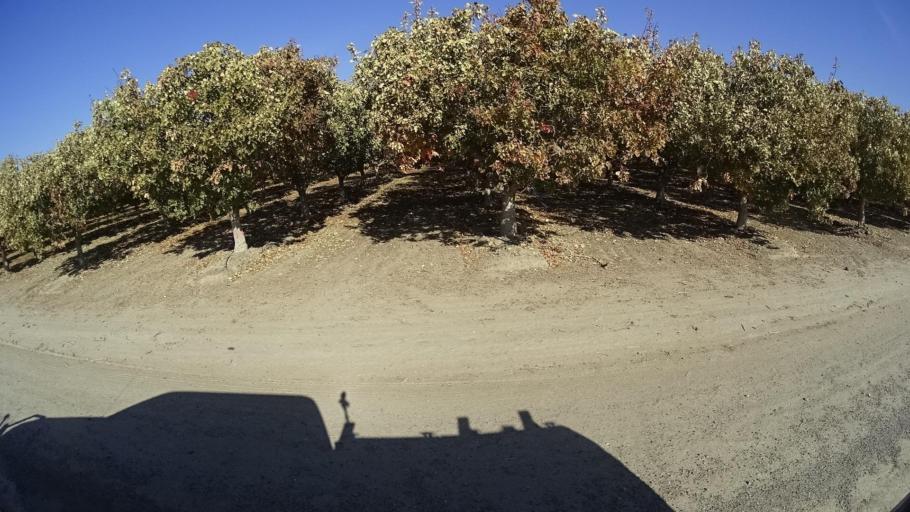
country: US
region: California
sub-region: Kern County
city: Wasco
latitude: 35.7176
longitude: -119.3961
